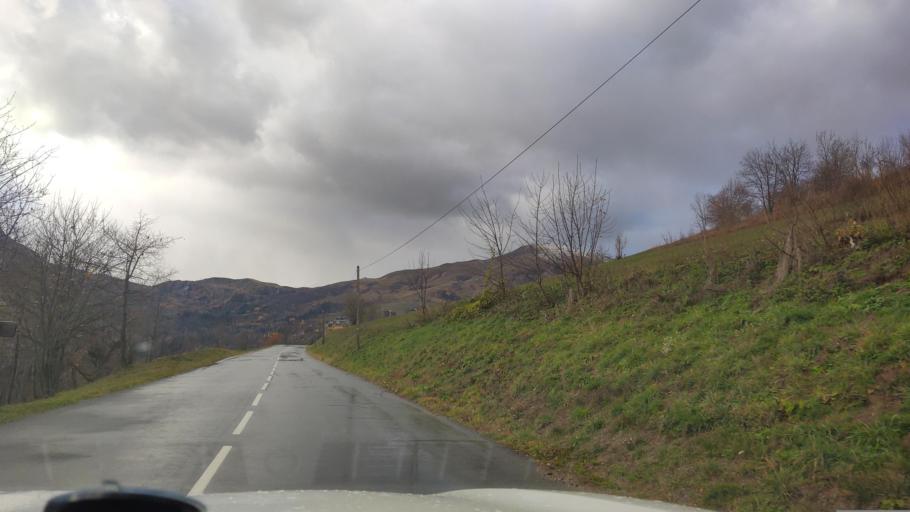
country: FR
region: Rhone-Alpes
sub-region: Departement de la Savoie
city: Saint-Jean-de-Maurienne
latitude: 45.2552
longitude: 6.3015
